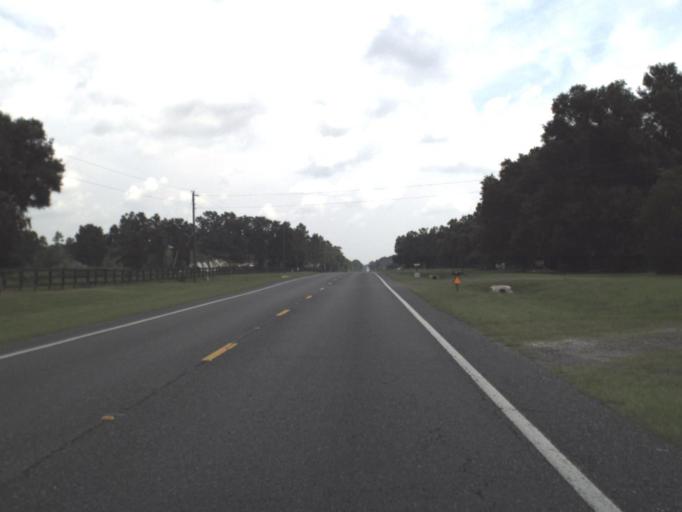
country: US
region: Florida
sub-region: Alachua County
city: High Springs
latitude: 29.8800
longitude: -82.6089
